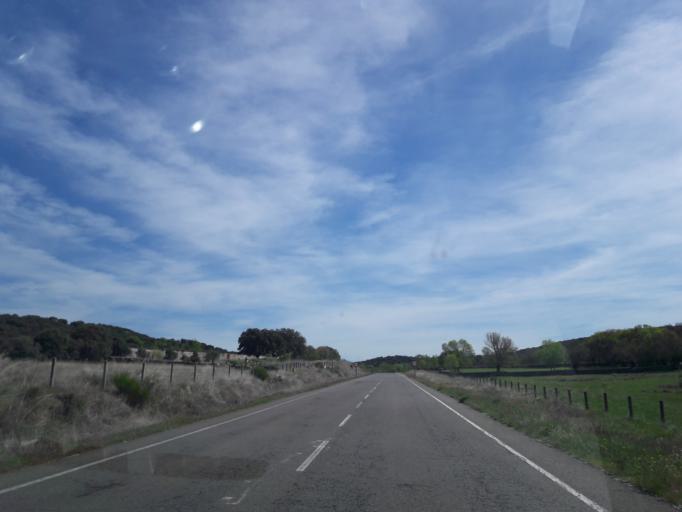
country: ES
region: Castille and Leon
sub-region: Provincia de Salamanca
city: Fuentes de Bejar
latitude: 40.4951
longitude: -5.7131
